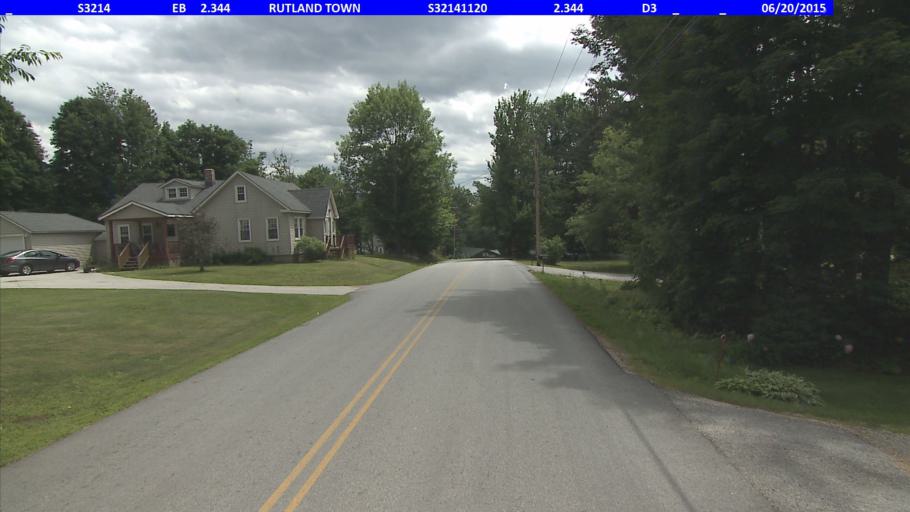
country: US
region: Vermont
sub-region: Rutland County
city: Rutland
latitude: 43.6319
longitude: -72.9435
